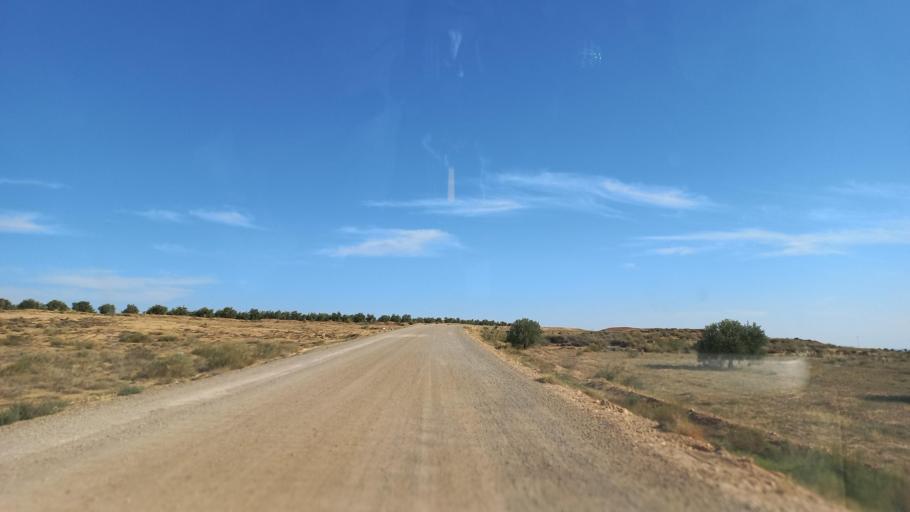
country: TN
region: Al Qasrayn
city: Sbiba
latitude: 35.3005
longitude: 9.0959
